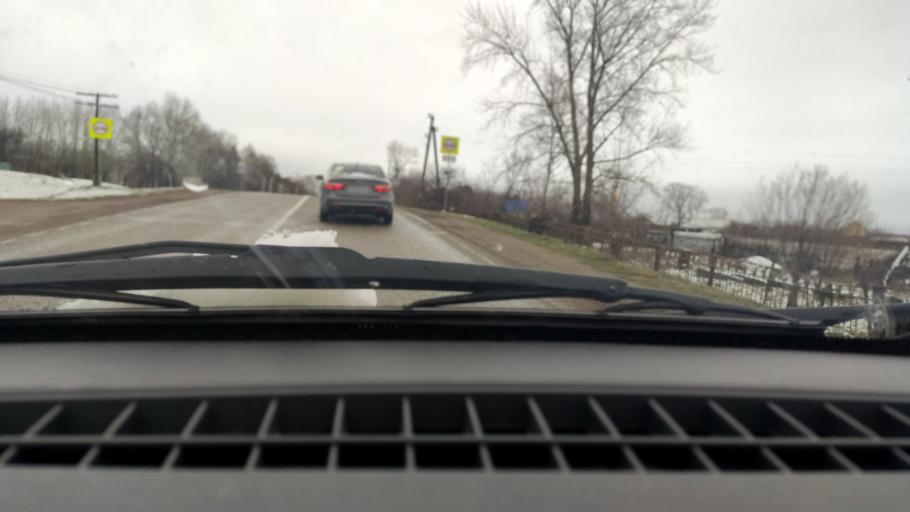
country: RU
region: Bashkortostan
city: Alekseyevka
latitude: 55.0517
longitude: 55.1301
